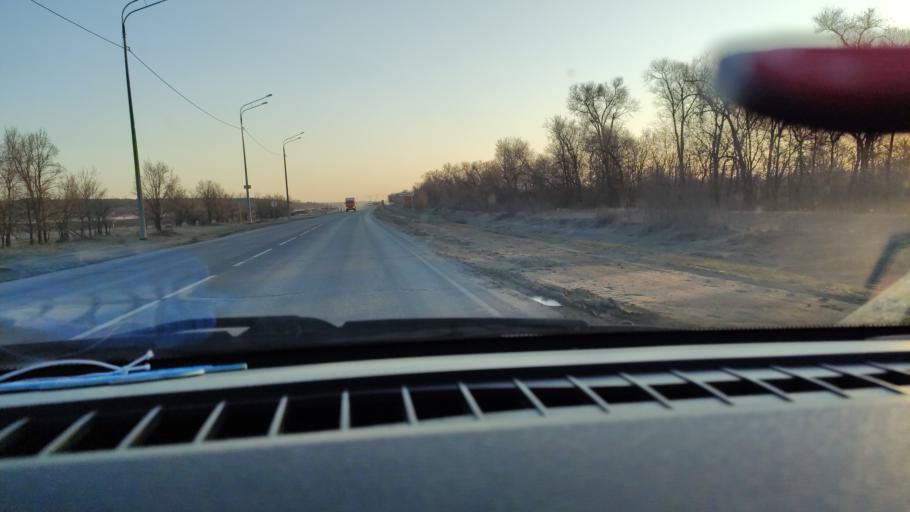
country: RU
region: Saratov
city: Sinodskoye
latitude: 51.9987
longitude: 46.6762
